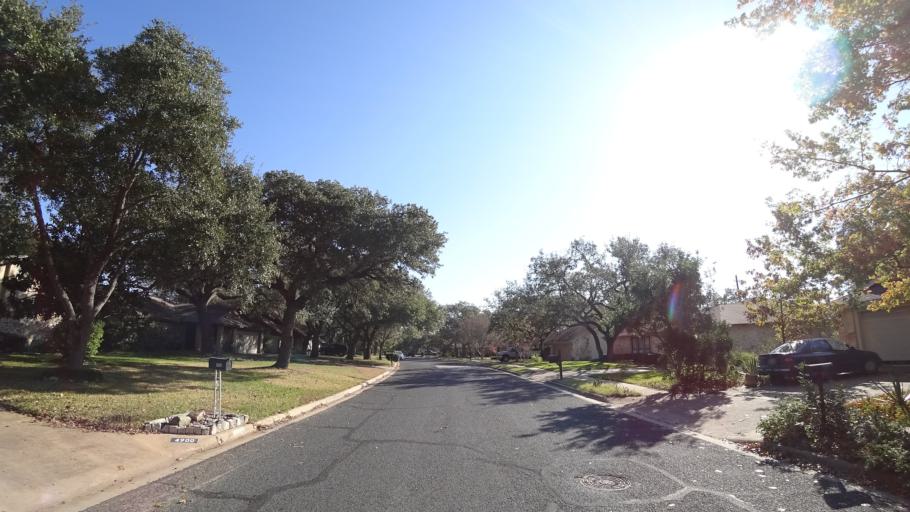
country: US
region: Texas
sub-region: Travis County
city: Barton Creek
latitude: 30.2264
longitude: -97.8453
